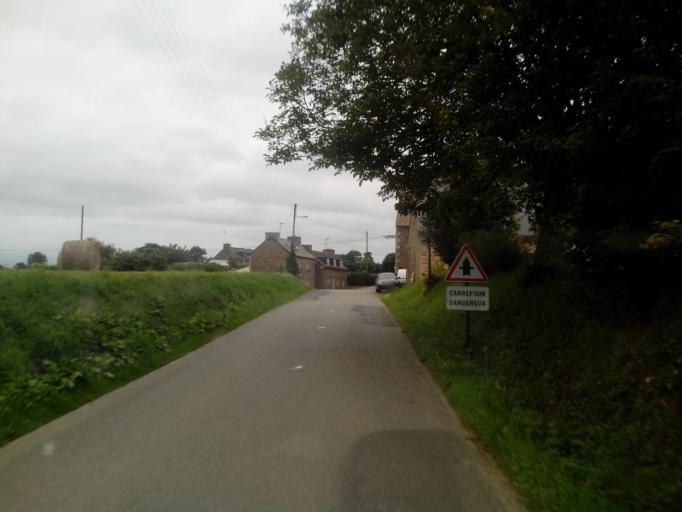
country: FR
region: Brittany
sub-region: Departement des Cotes-d'Armor
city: Plehedel
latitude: 48.6849
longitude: -2.9741
